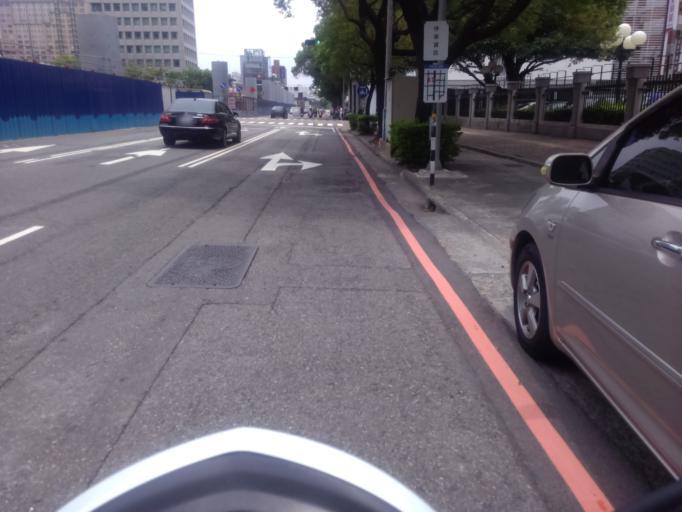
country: TW
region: Taiwan
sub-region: Taichung City
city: Taichung
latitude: 24.1597
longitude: 120.6480
